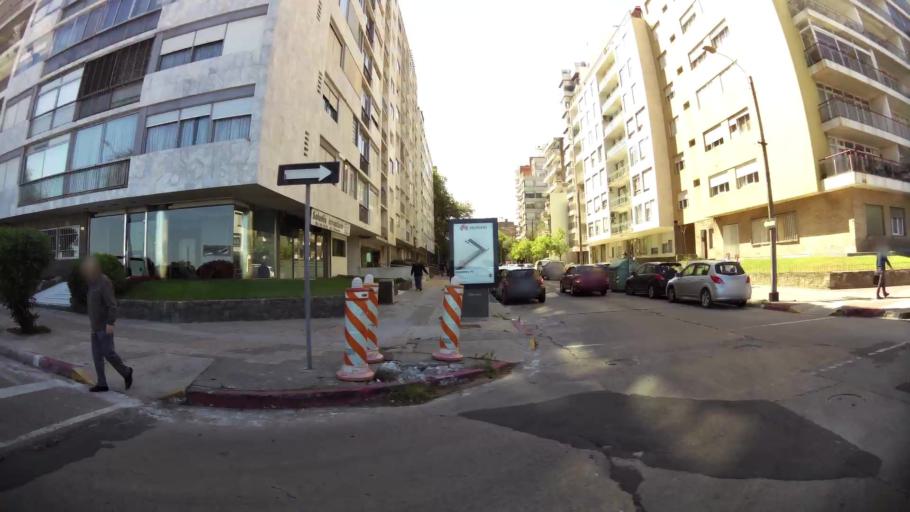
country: UY
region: Montevideo
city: Montevideo
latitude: -34.9101
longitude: -56.1444
